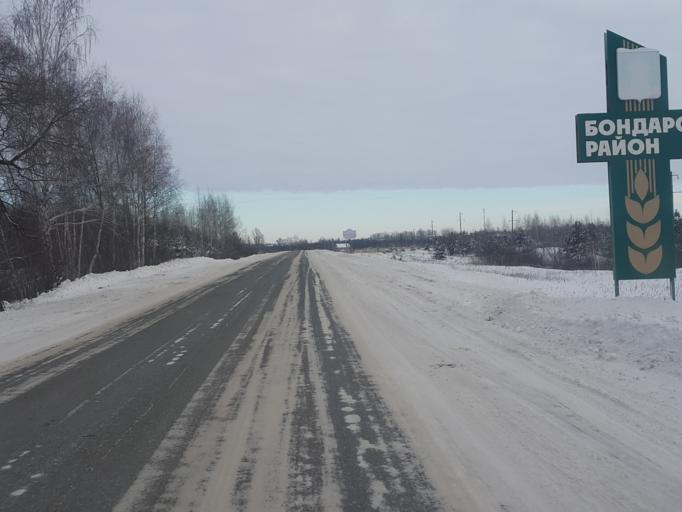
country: RU
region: Tambov
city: Platonovka
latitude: 52.8686
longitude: 41.8608
